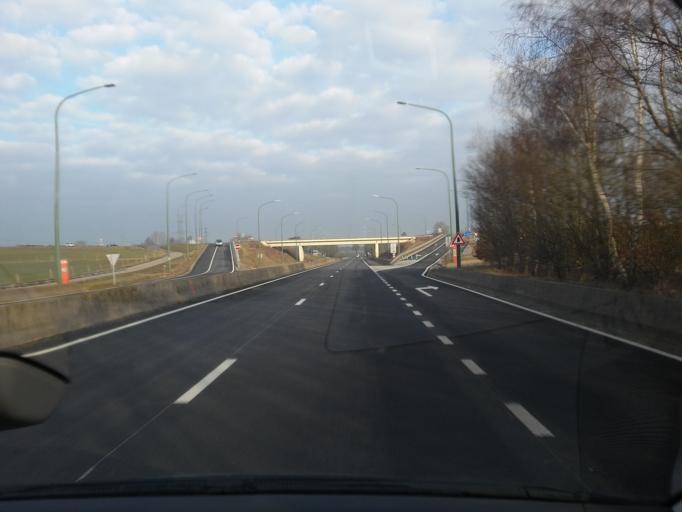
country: BE
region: Wallonia
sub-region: Province du Luxembourg
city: Martelange
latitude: 49.8626
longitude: 5.7200
